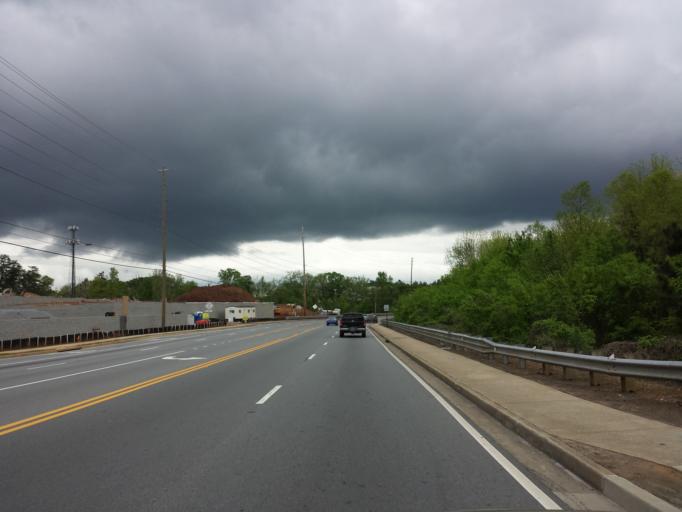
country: US
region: Georgia
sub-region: Cobb County
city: Kennesaw
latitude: 34.0248
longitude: -84.5752
